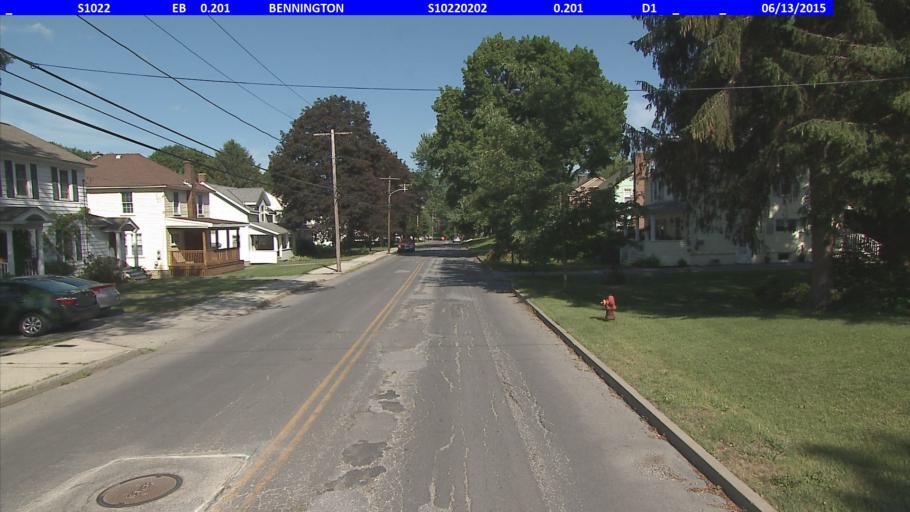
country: US
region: Vermont
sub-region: Bennington County
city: Bennington
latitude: 42.8780
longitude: -73.2059
